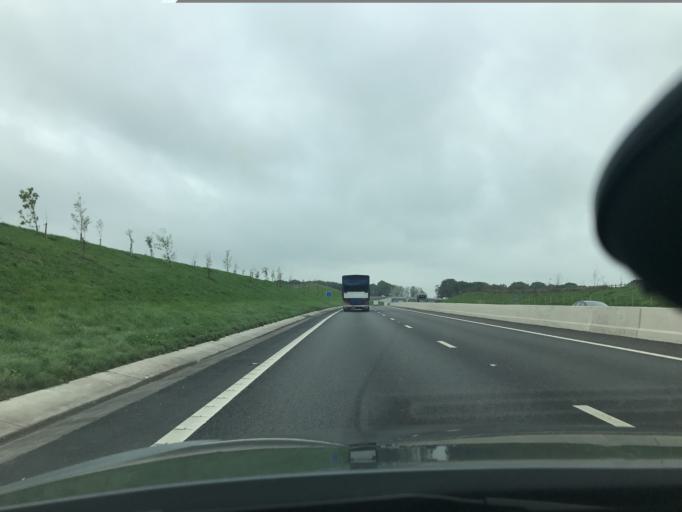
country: GB
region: England
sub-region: Cheshire East
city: Mere
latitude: 53.3412
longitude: -2.4149
